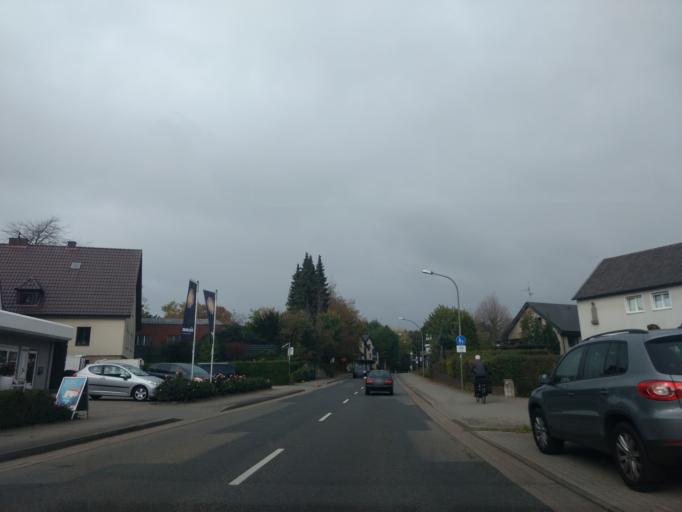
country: DE
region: Lower Saxony
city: Bad Iburg
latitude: 52.1460
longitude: 8.0530
